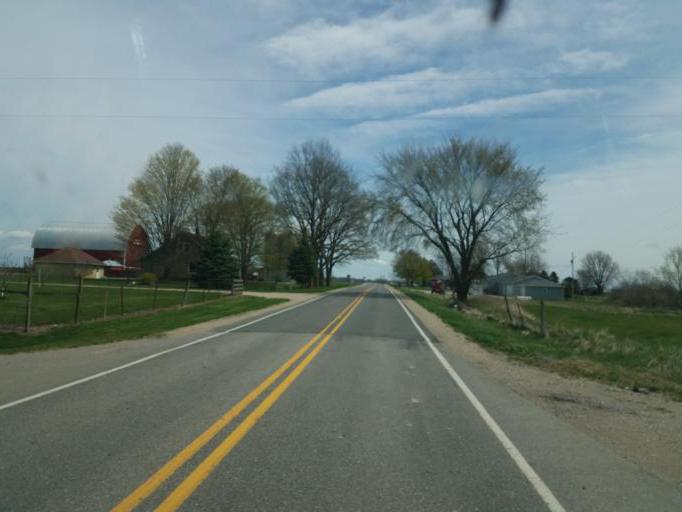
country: US
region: Michigan
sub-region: Isabella County
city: Lake Isabella
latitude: 43.6269
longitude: -84.8833
